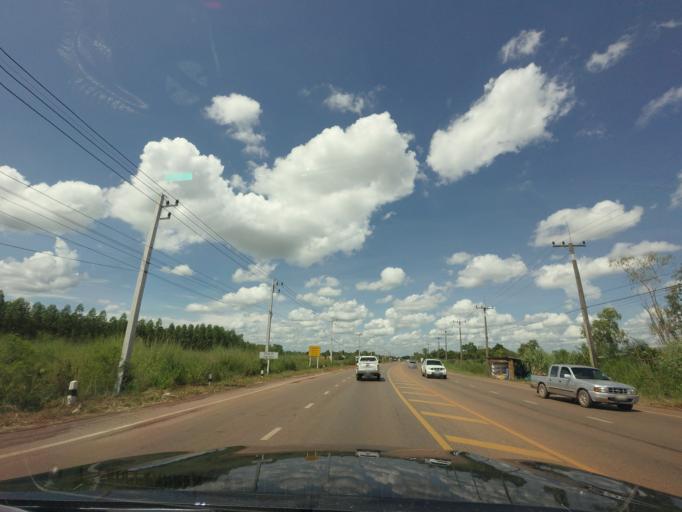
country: TH
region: Changwat Udon Thani
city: Ban Dung
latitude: 17.7219
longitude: 103.2502
